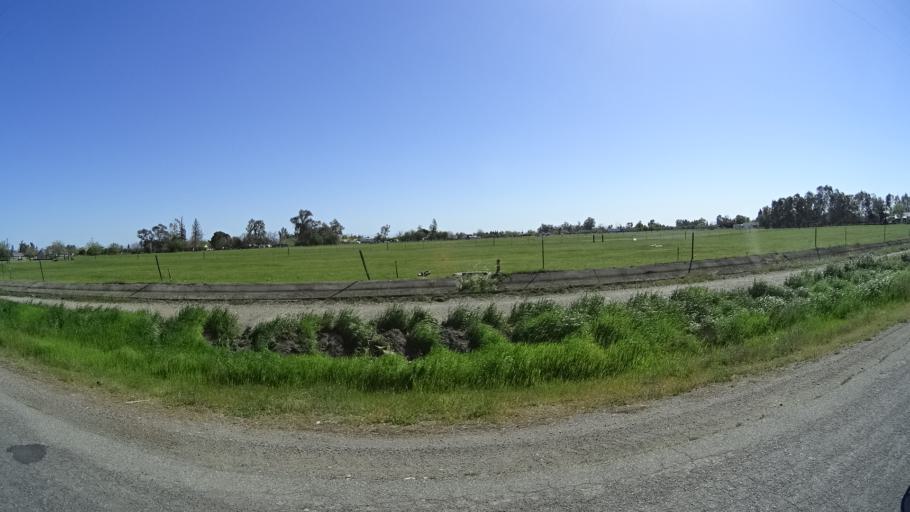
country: US
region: California
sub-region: Glenn County
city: Orland
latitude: 39.7199
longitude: -122.2119
